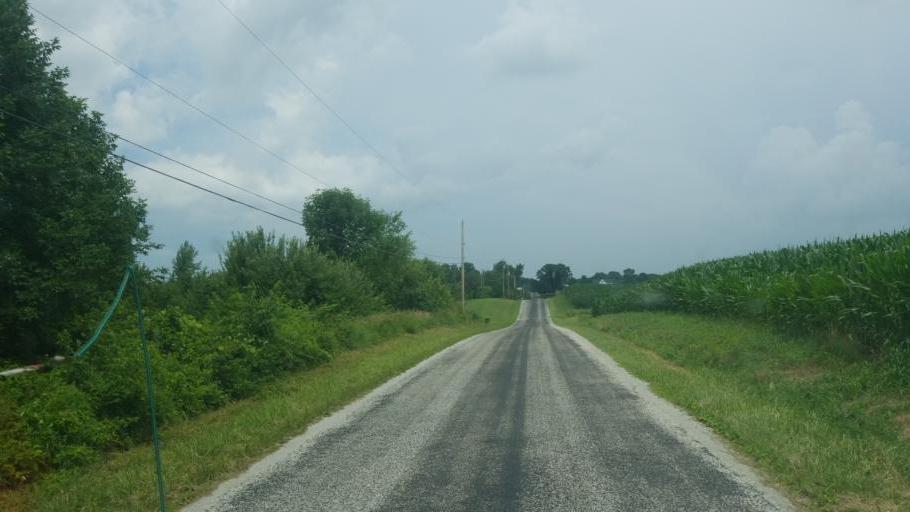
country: US
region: Ohio
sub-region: Wayne County
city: West Salem
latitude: 40.8512
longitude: -82.1256
